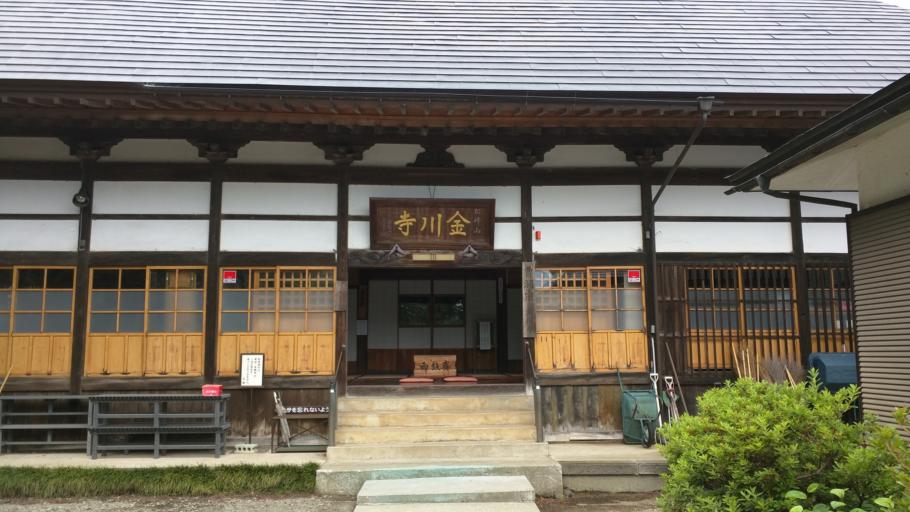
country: JP
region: Fukushima
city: Kitakata
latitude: 37.5867
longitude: 139.9084
